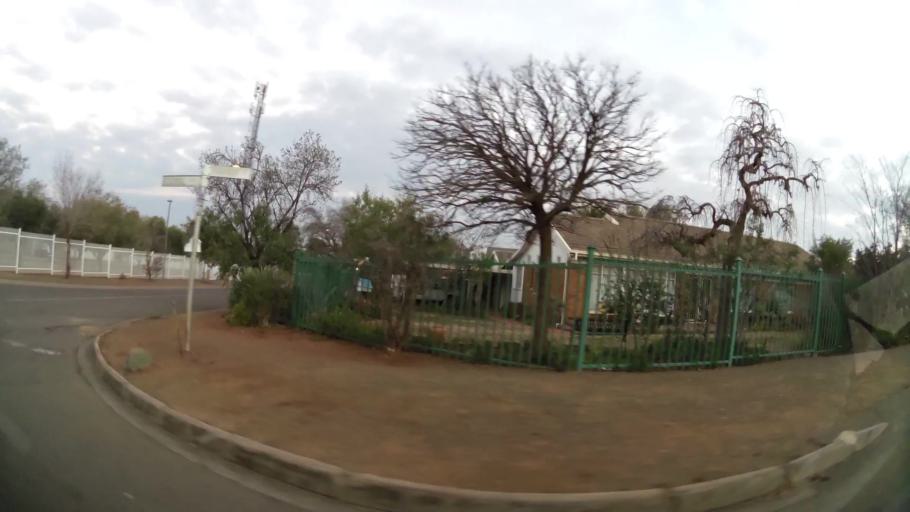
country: ZA
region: Orange Free State
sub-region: Mangaung Metropolitan Municipality
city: Bloemfontein
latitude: -29.1644
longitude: 26.1966
